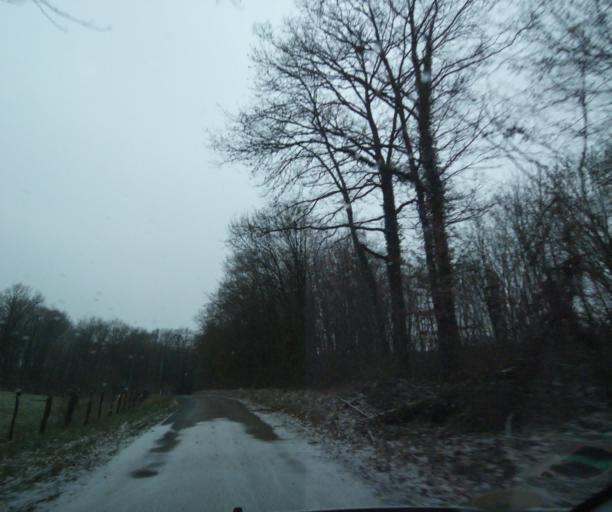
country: FR
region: Champagne-Ardenne
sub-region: Departement de la Haute-Marne
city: Wassy
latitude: 48.4645
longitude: 5.0171
